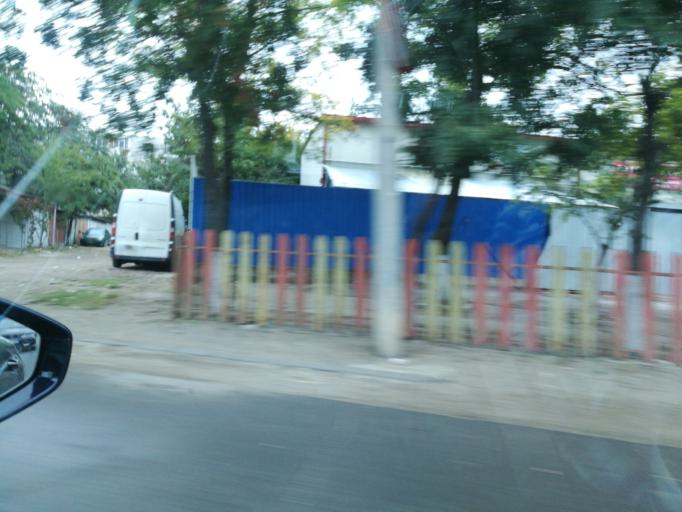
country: RO
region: Galati
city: Galati
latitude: 45.4494
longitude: 28.0148
